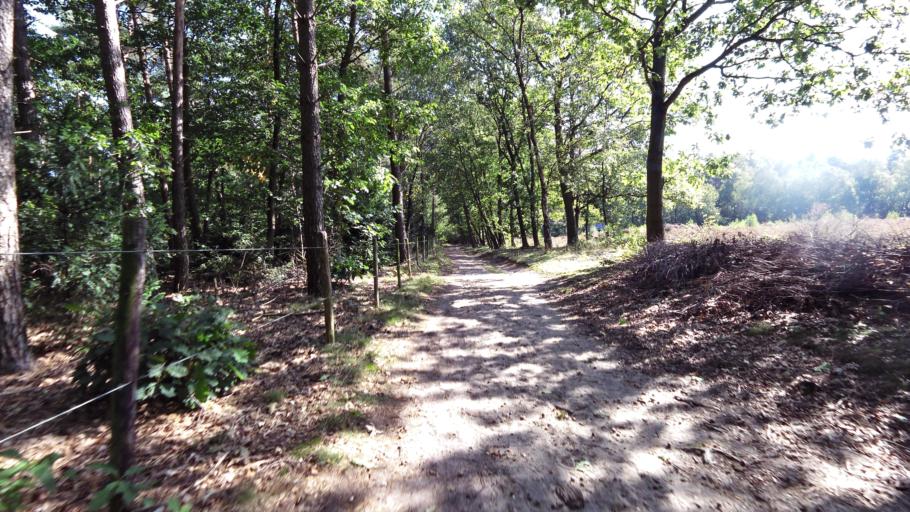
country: NL
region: Gelderland
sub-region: Gemeente Renkum
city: Renkum
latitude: 52.0130
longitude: 5.7249
